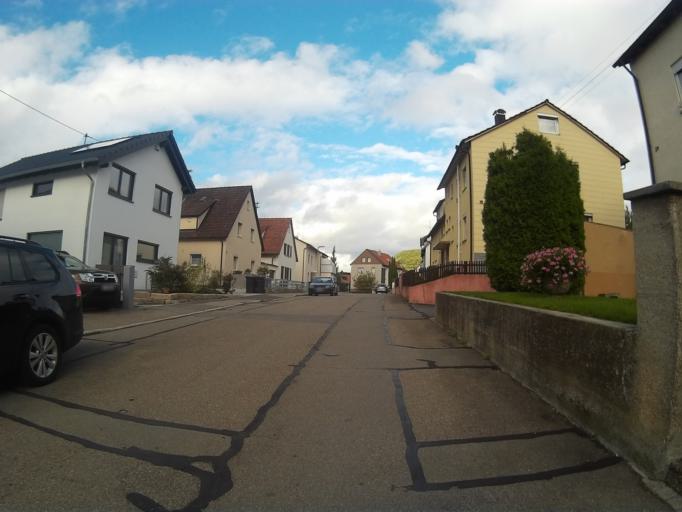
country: DE
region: Baden-Wuerttemberg
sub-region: Tuebingen Region
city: Pfullingen
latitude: 48.4551
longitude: 9.2221
